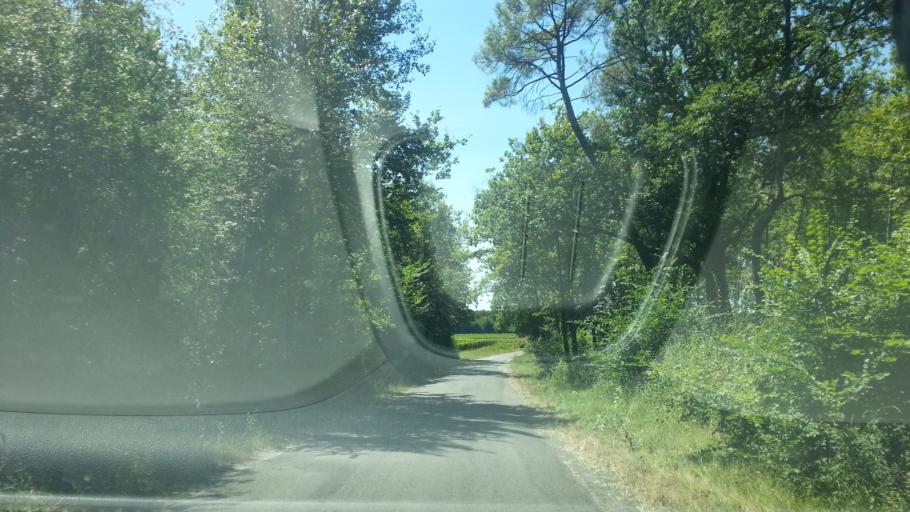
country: FR
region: Aquitaine
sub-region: Departement de la Gironde
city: Landiras
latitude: 44.5741
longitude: -0.3948
